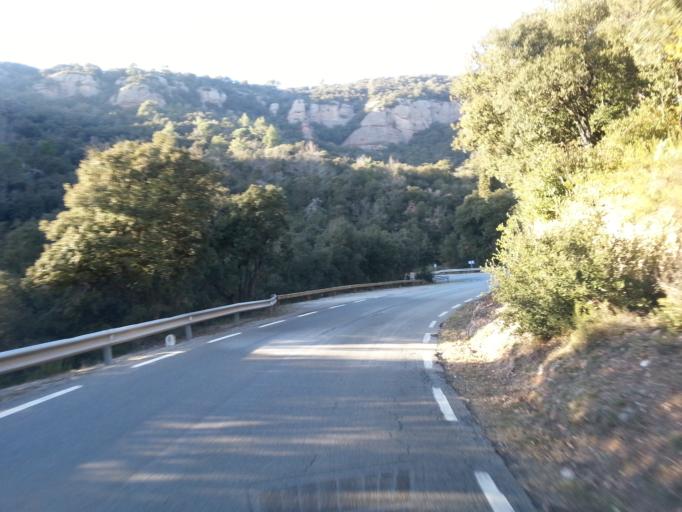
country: ES
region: Catalonia
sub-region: Provincia de Barcelona
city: Mura
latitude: 41.6575
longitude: 1.9839
